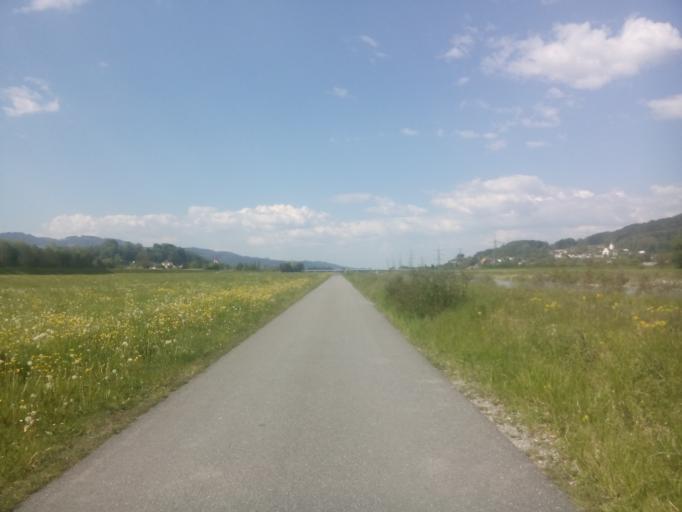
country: AT
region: Vorarlberg
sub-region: Politischer Bezirk Feldkirch
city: Koblach
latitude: 47.3234
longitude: 9.5902
